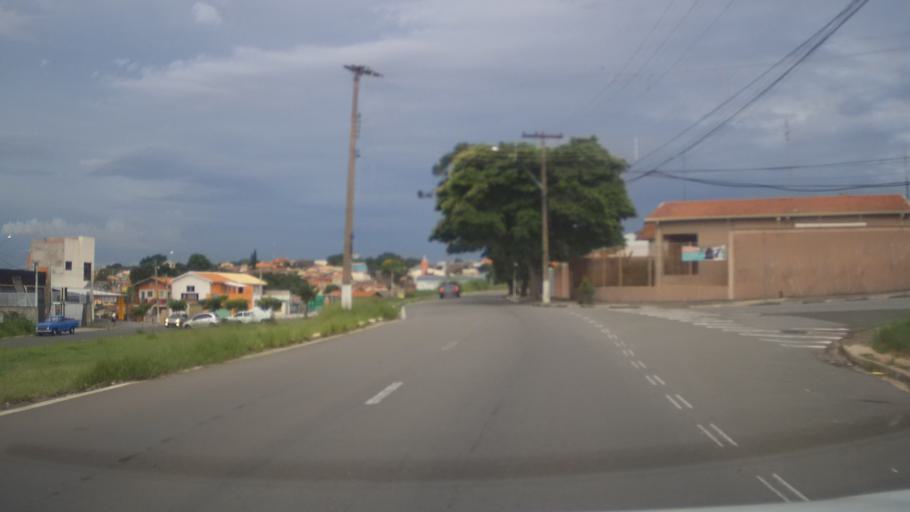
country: BR
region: Sao Paulo
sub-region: Campinas
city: Campinas
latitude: -22.9314
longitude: -47.1178
